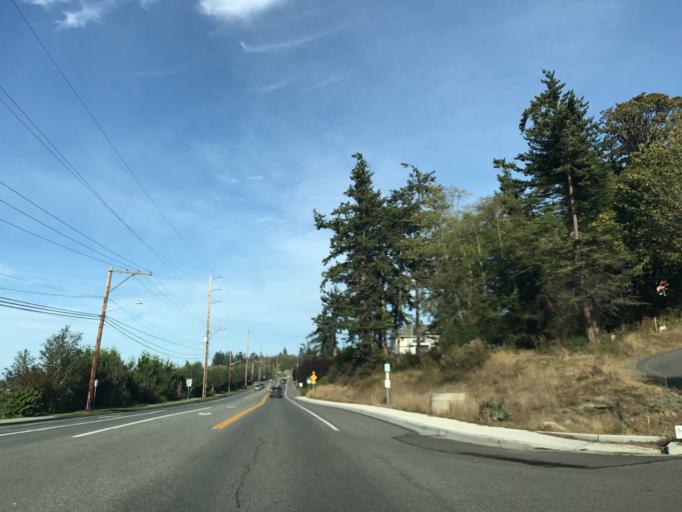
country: US
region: Washington
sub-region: Skagit County
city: Anacortes
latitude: 48.5009
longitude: -122.6701
